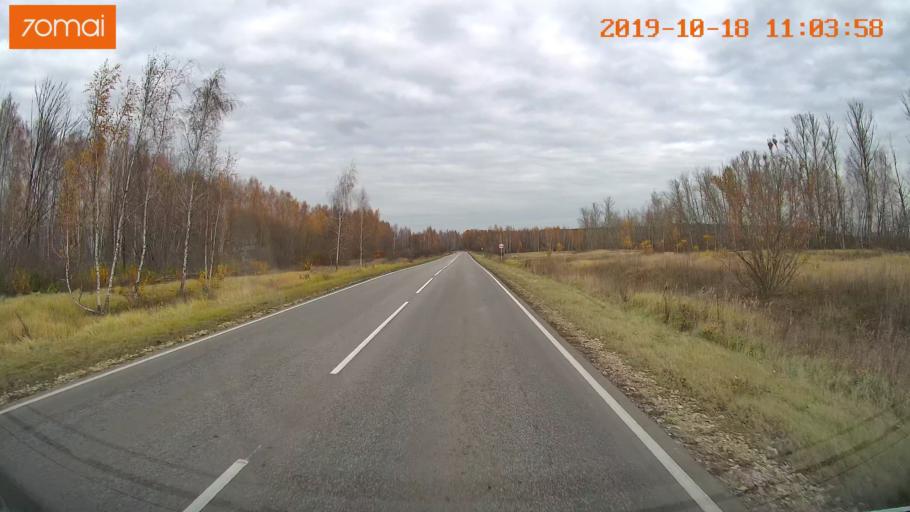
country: RU
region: Tula
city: Yepifan'
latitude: 53.8877
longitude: 38.5500
